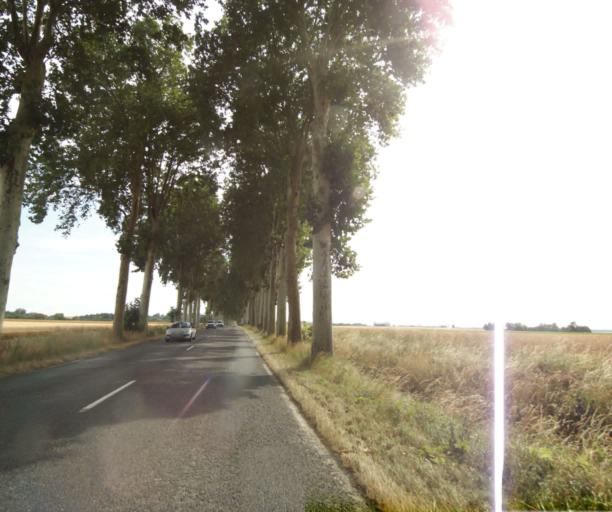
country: FR
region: Ile-de-France
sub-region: Departement de Seine-et-Marne
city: La Chapelle-la-Reine
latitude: 48.3315
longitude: 2.5896
